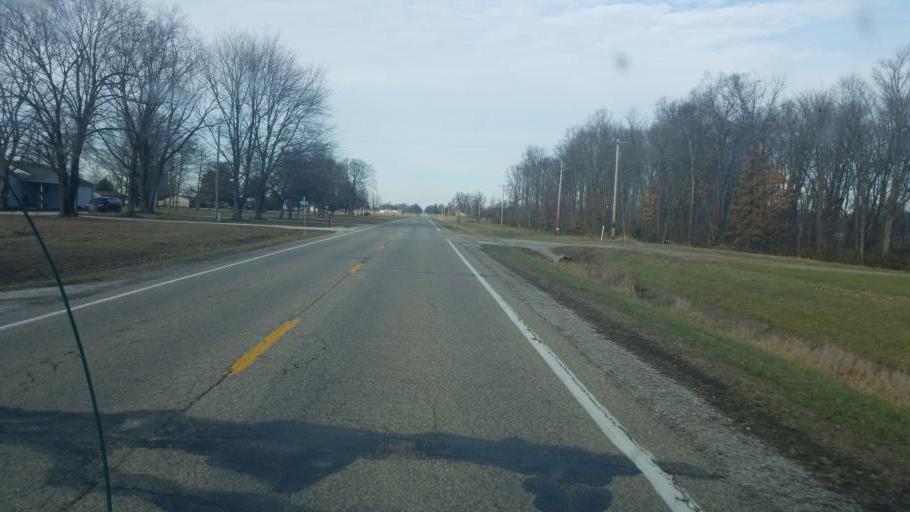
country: US
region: Illinois
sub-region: Lawrence County
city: Bridgeport
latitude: 38.5714
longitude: -87.6946
